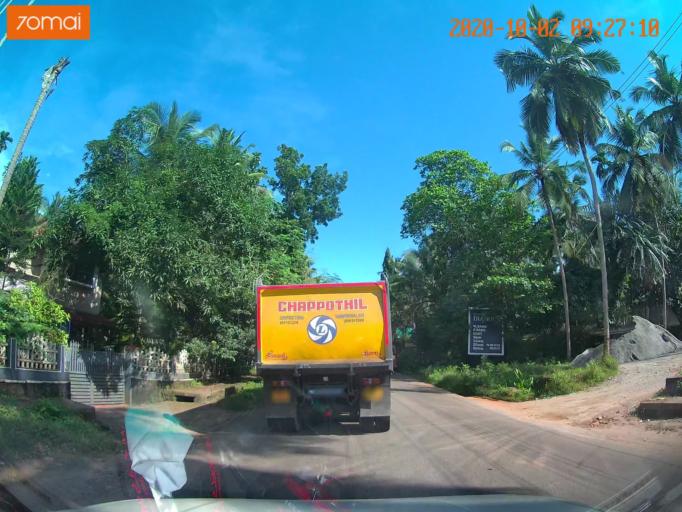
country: IN
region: Kerala
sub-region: Kozhikode
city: Naduvannur
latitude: 11.5970
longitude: 75.7650
